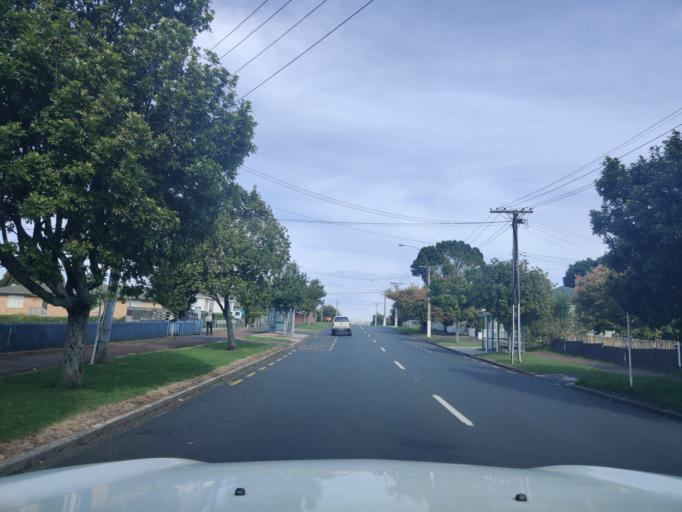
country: NZ
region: Auckland
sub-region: Auckland
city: Tamaki
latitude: -36.8990
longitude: 174.8592
